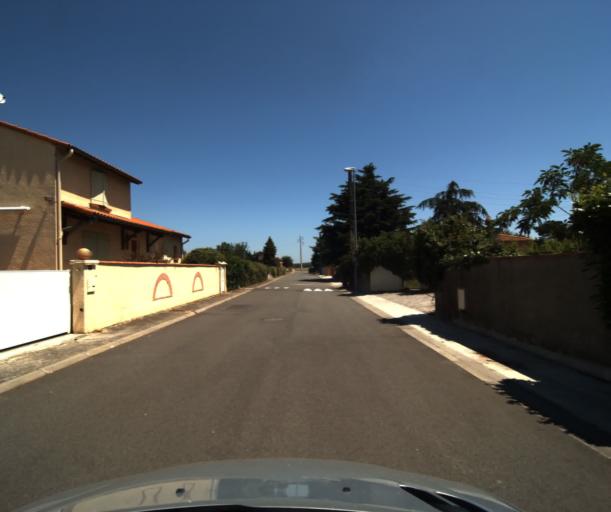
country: FR
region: Midi-Pyrenees
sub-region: Departement de la Haute-Garonne
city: Roquettes
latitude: 43.4960
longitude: 1.3792
